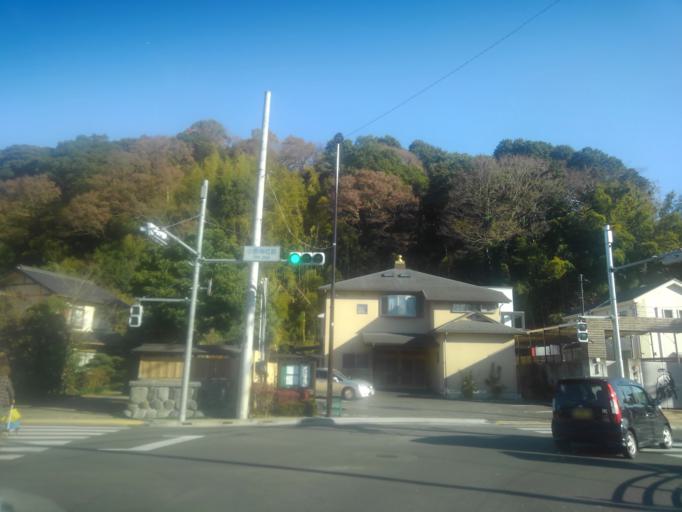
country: JP
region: Tokyo
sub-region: Machida-shi
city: Machida
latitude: 35.5982
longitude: 139.4389
